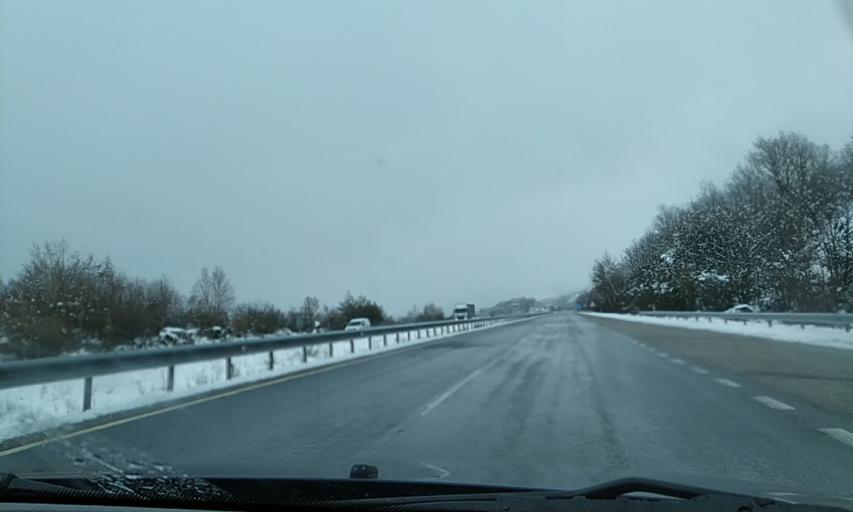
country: ES
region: Castille and Leon
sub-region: Provincia de Zamora
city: Lubian
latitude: 42.0291
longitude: -6.9100
